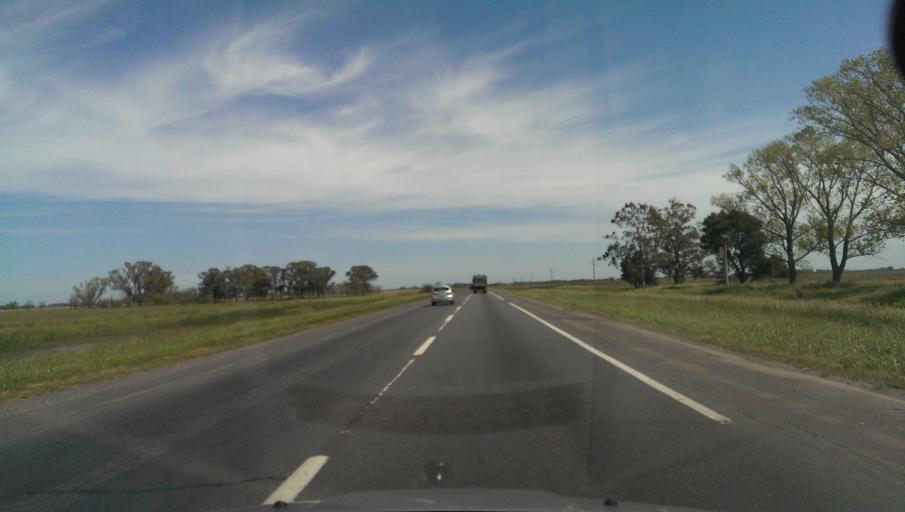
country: AR
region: Buenos Aires
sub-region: Partido de Las Flores
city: Las Flores
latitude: -35.9651
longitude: -59.0232
